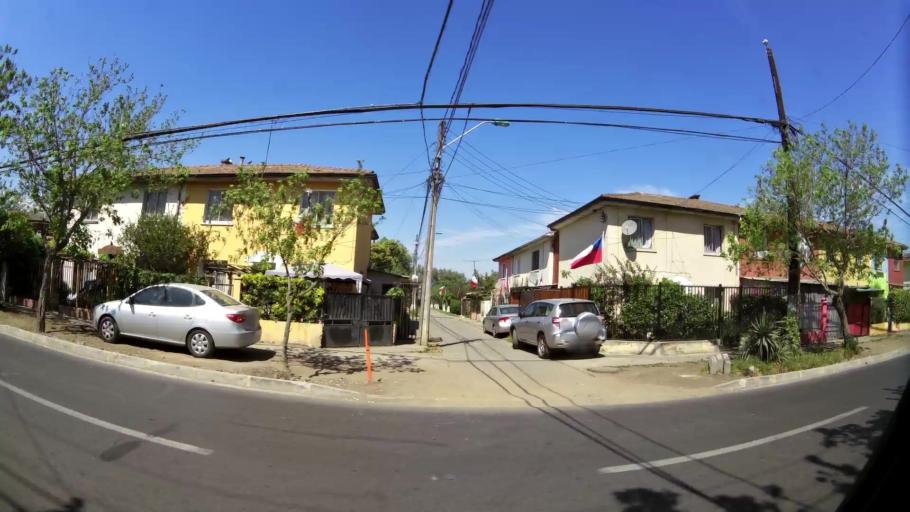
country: CL
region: Santiago Metropolitan
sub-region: Provincia de Talagante
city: Talagante
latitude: -33.6579
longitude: -70.9133
